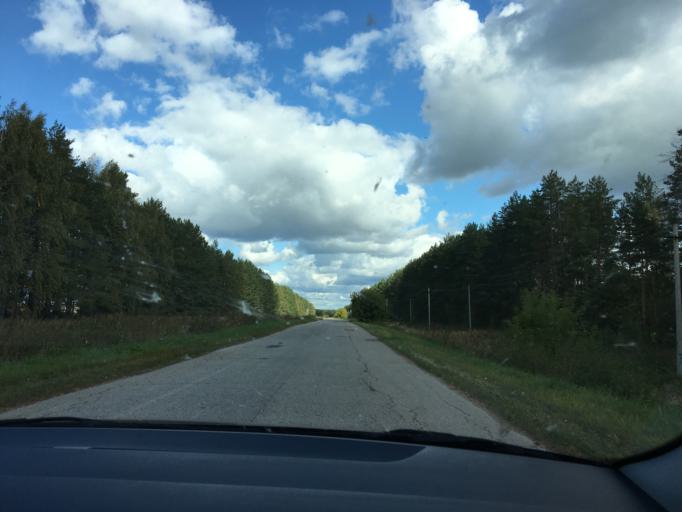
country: RU
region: Nizjnij Novgorod
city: Spasskoye
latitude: 56.0542
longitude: 45.4776
